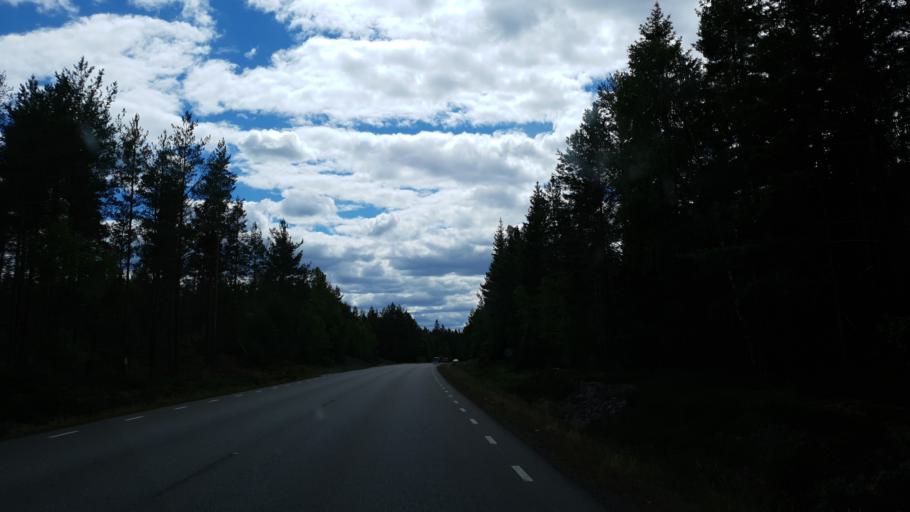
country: SE
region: Kronoberg
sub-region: Uppvidinge Kommun
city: Lenhovda
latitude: 56.9371
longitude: 15.5822
